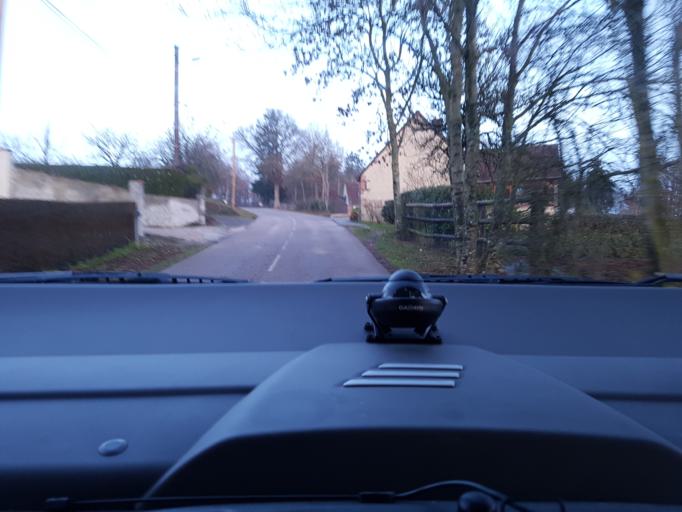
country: FR
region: Lower Normandy
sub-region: Departement de l'Orne
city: Tourouvre
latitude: 48.6006
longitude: 0.6673
